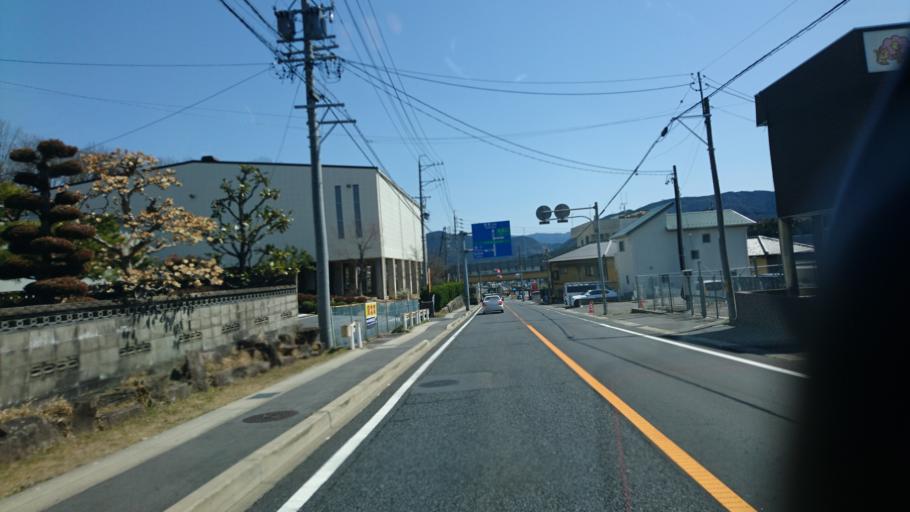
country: JP
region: Gifu
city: Nakatsugawa
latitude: 35.4558
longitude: 137.3958
